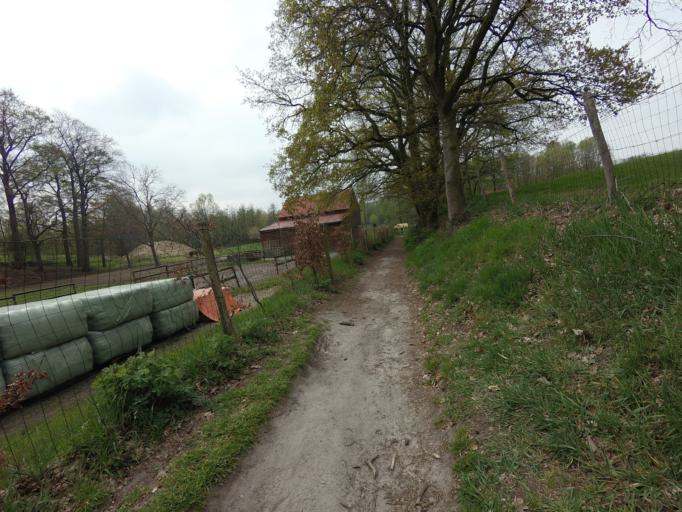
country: NL
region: Limburg
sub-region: Gemeente Schinnen
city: Schinnen
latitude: 50.9401
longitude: 5.8937
